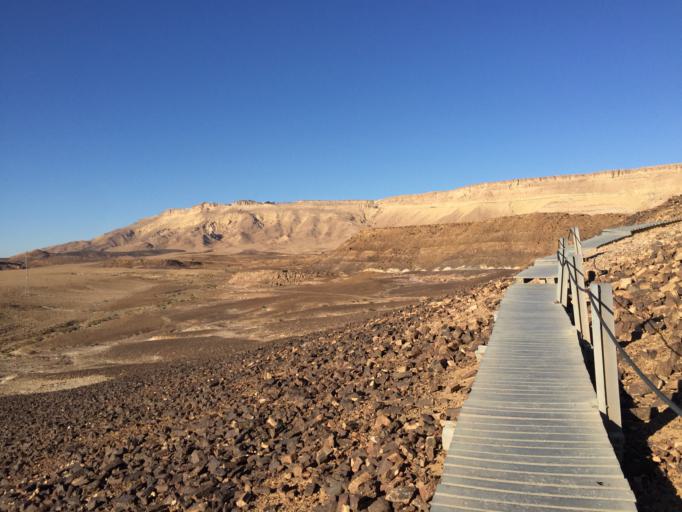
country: IL
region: Southern District
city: Mitzpe Ramon
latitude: 30.6153
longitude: 34.8388
